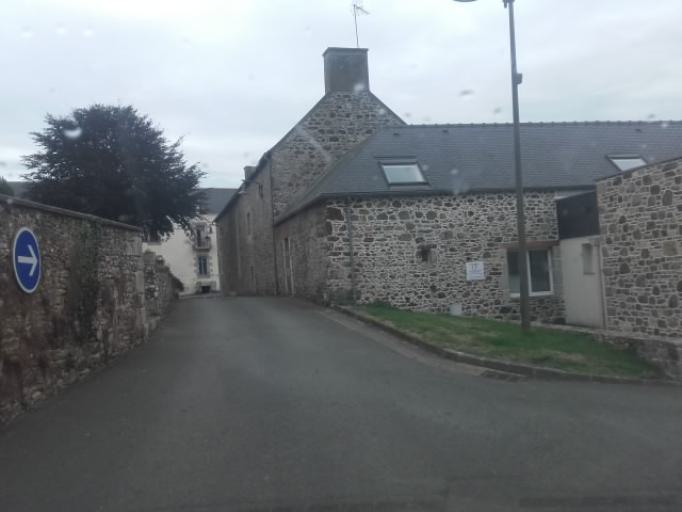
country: FR
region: Brittany
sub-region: Departement des Cotes-d'Armor
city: Pleguien
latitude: 48.6359
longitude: -2.9407
